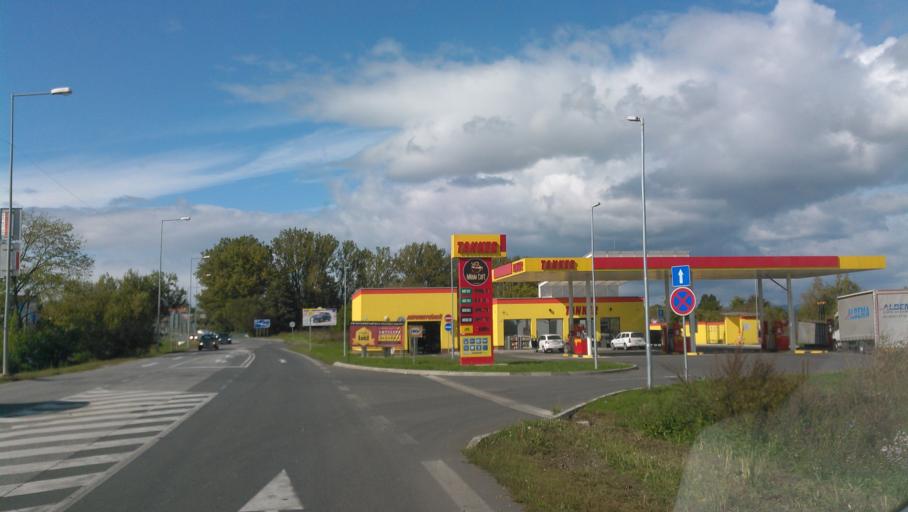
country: SK
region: Banskobystricky
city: Rimavska Sobota
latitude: 48.3878
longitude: 19.9990
